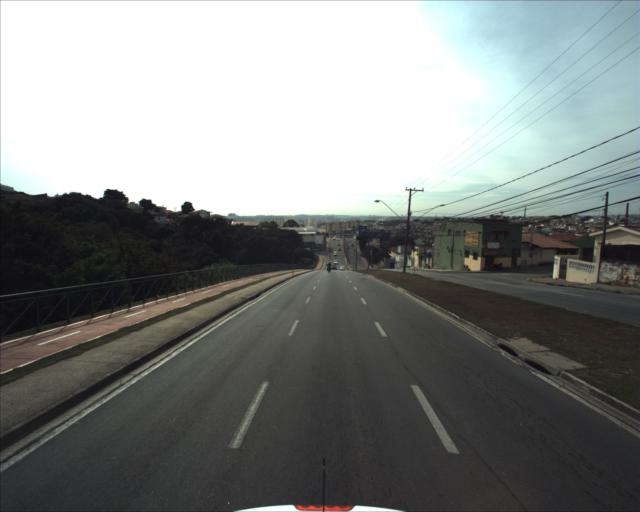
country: BR
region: Sao Paulo
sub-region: Sorocaba
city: Sorocaba
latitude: -23.4839
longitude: -47.4654
